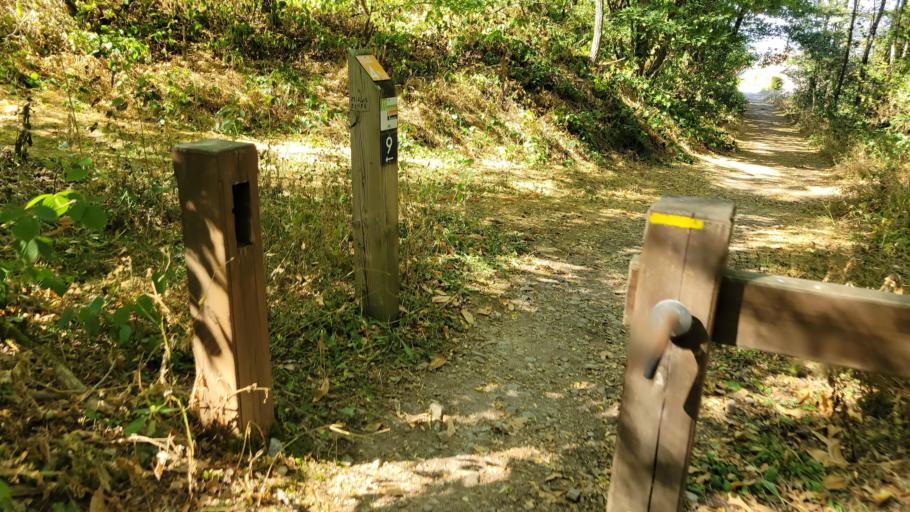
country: FR
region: Bourgogne
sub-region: Departement de Saone-et-Loire
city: Autun
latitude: 46.9380
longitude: 4.3167
